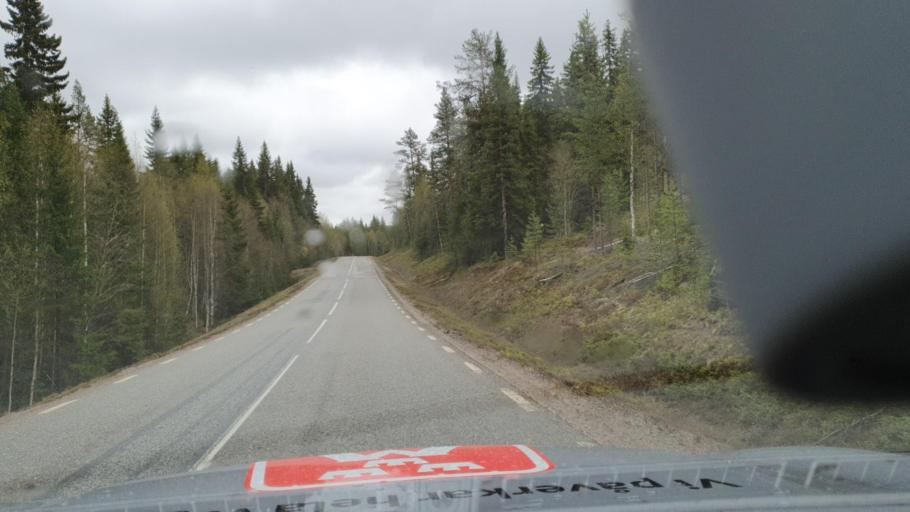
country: SE
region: Vaesterbotten
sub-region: Asele Kommun
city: Asele
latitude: 63.7049
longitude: 17.1974
